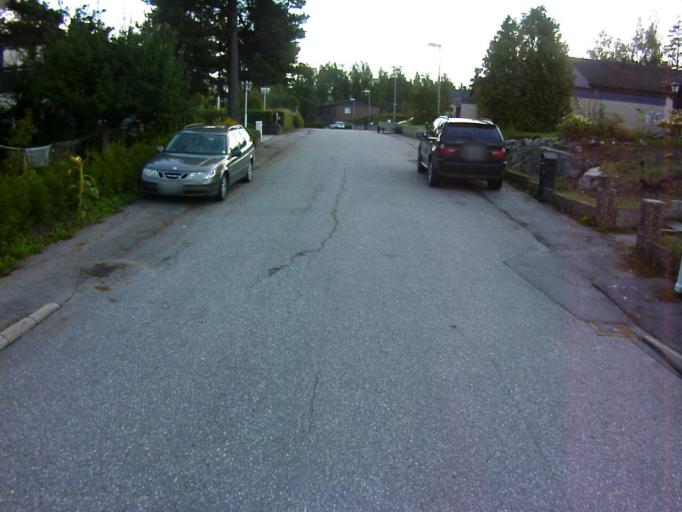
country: SE
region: Soedermanland
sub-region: Eskilstuna Kommun
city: Eskilstuna
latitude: 59.3988
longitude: 16.5362
